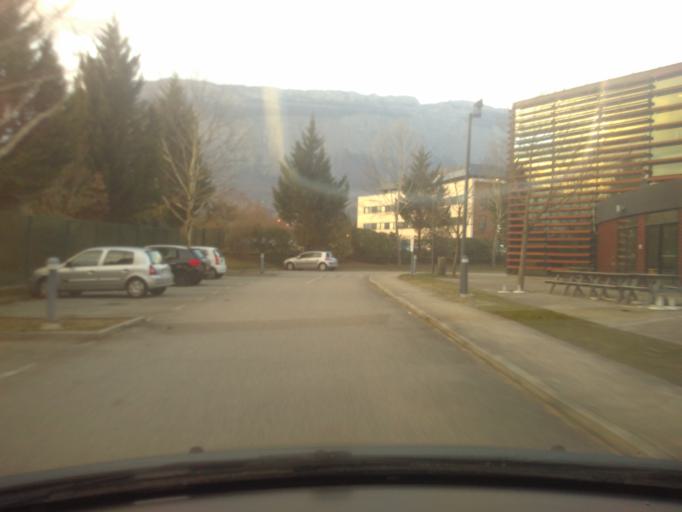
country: FR
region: Rhone-Alpes
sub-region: Departement de l'Isere
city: Montbonnot-Saint-Martin
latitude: 45.2132
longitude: 5.8060
